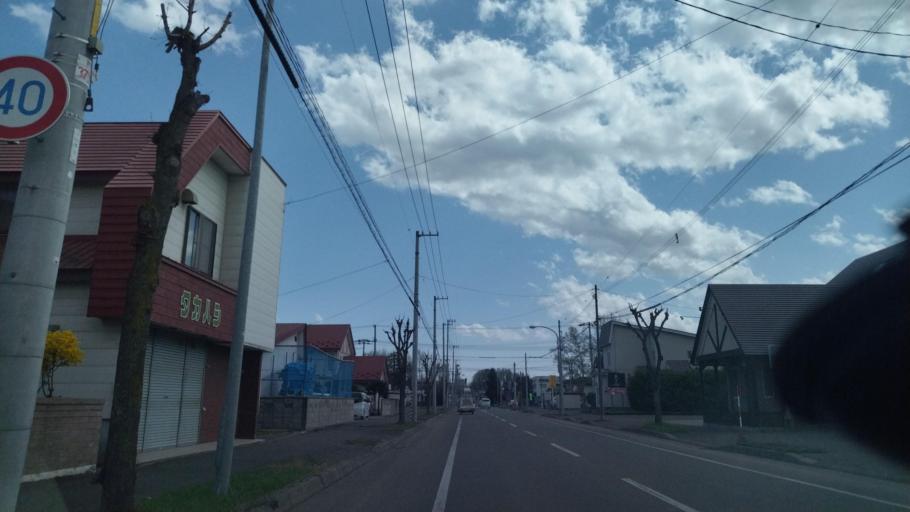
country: JP
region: Hokkaido
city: Obihiro
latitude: 42.9095
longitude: 143.1524
